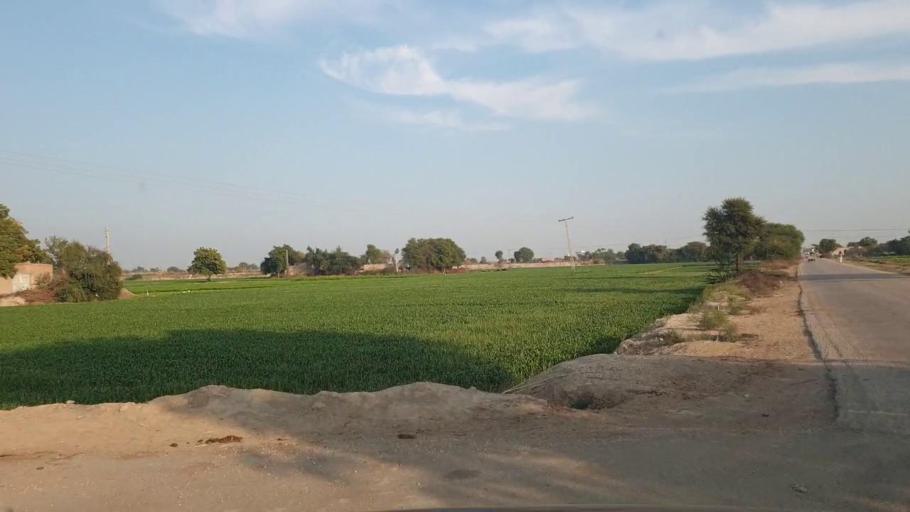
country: PK
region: Sindh
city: Shahpur Chakar
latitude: 26.1602
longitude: 68.6365
